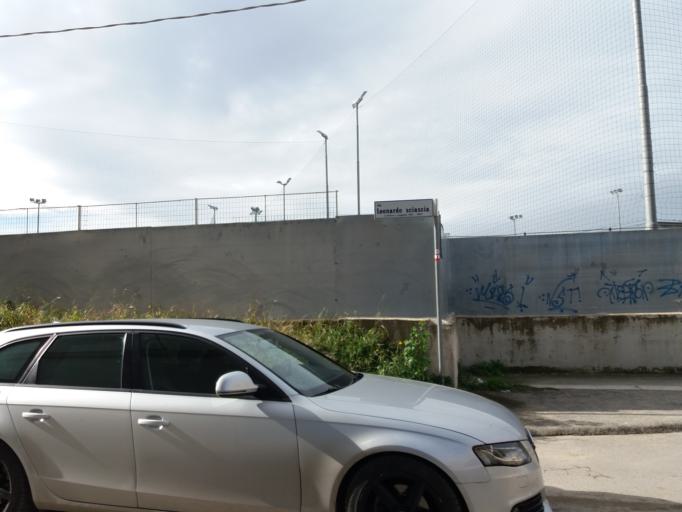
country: IT
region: Apulia
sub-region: Provincia di Barletta - Andria - Trani
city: Andria
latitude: 41.2176
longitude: 16.3054
